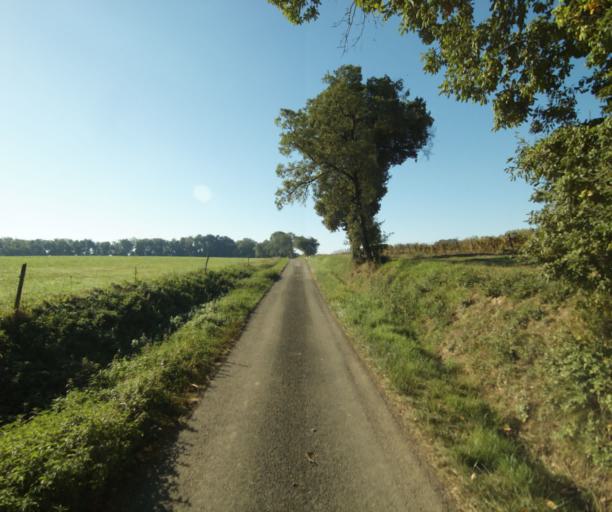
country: FR
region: Midi-Pyrenees
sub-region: Departement du Gers
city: Vic-Fezensac
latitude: 43.8247
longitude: 0.2822
